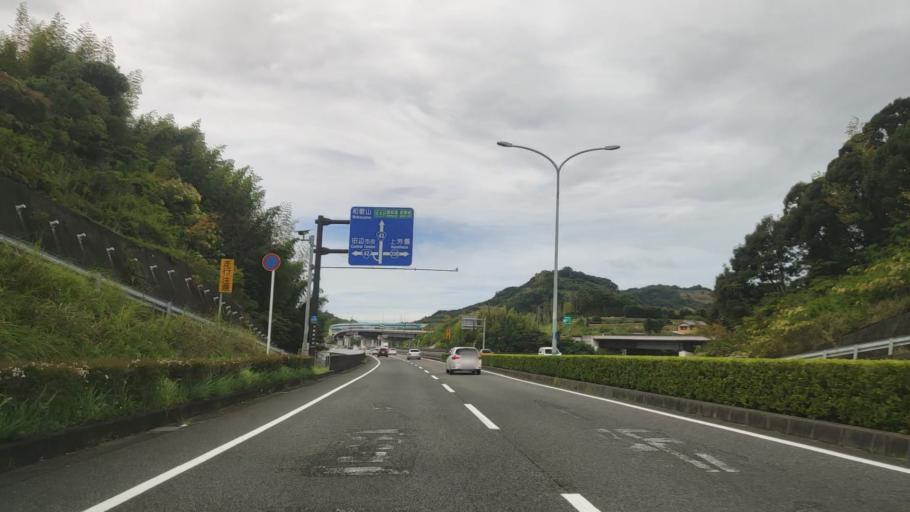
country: JP
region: Wakayama
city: Tanabe
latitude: 33.7450
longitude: 135.3803
